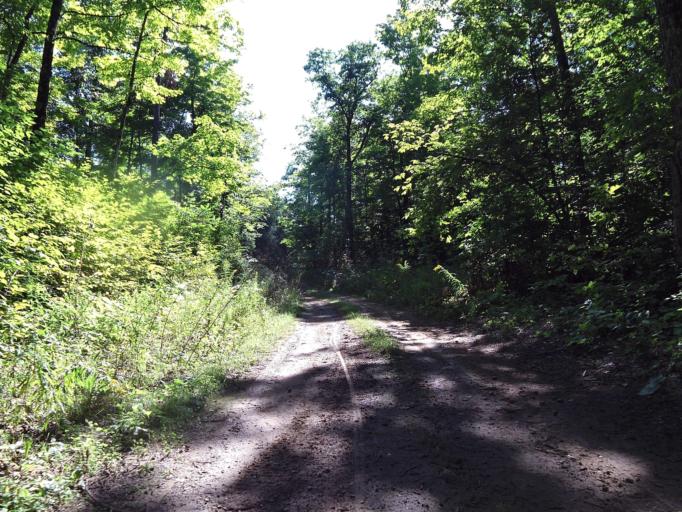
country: CA
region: Ontario
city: Renfrew
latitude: 45.1278
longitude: -76.7354
